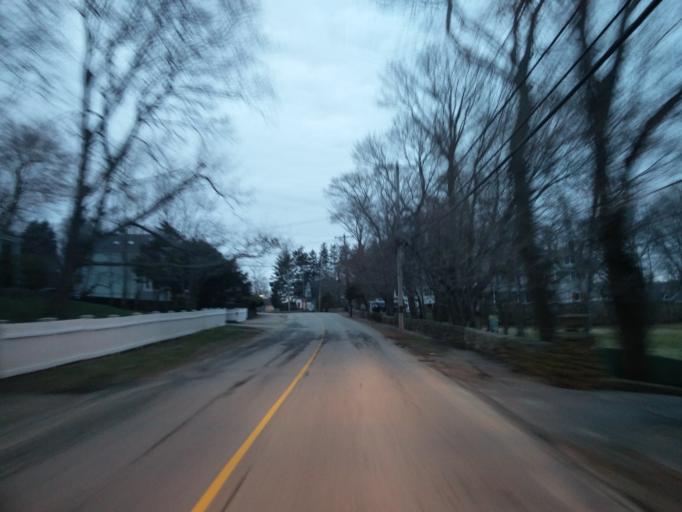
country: US
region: Massachusetts
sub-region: Norfolk County
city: Cohasset
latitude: 42.2626
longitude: -70.8356
